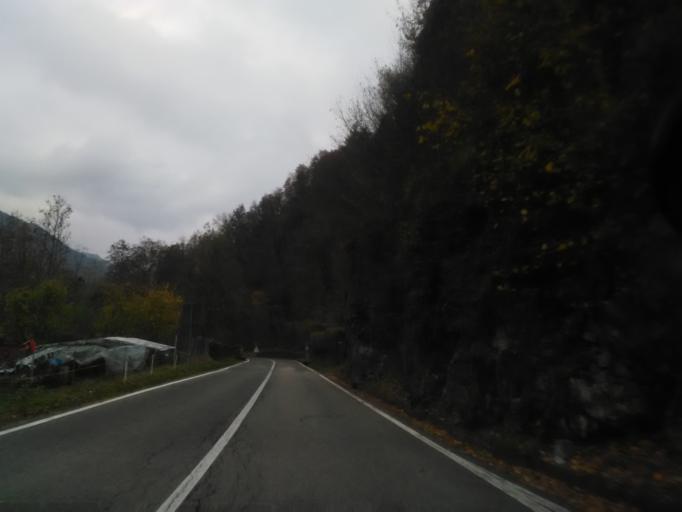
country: IT
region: Piedmont
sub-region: Provincia di Vercelli
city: Varallo
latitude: 45.8034
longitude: 8.2592
